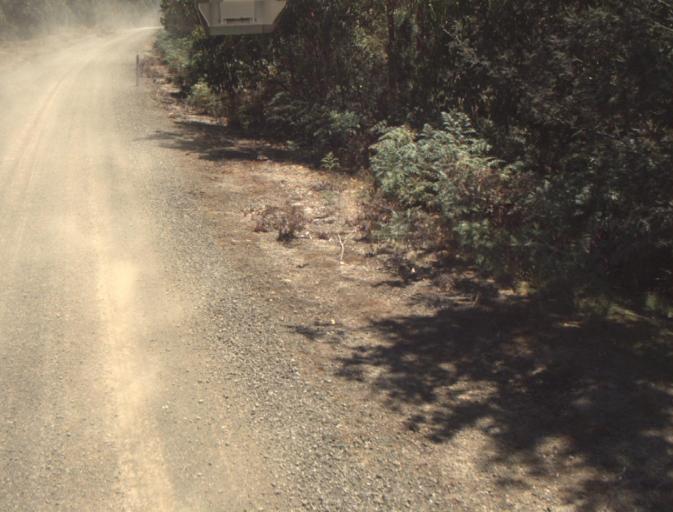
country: AU
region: Tasmania
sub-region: Dorset
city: Scottsdale
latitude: -41.2930
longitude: 147.3482
